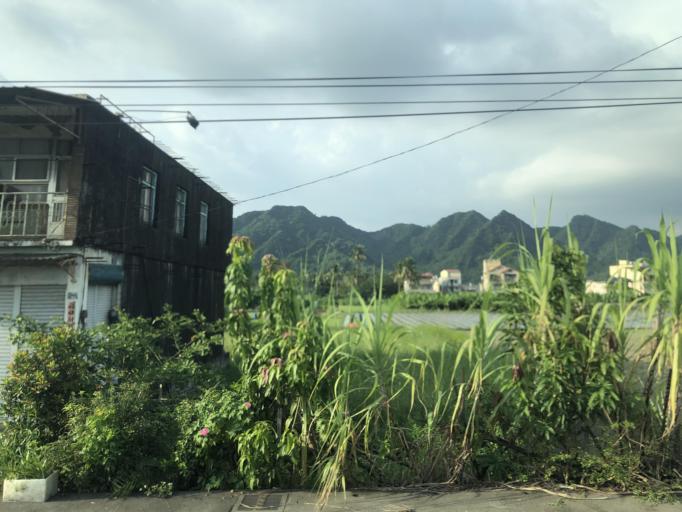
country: TW
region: Taiwan
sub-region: Pingtung
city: Pingtung
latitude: 22.8852
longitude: 120.5078
